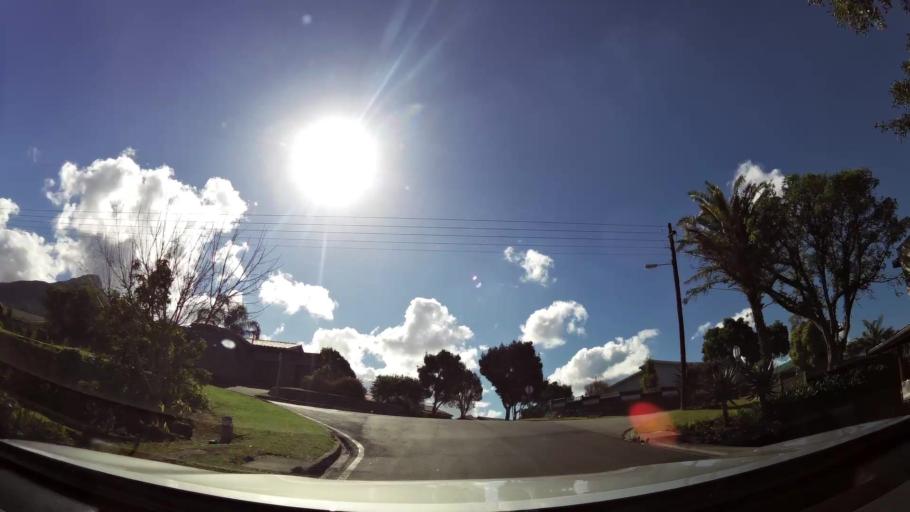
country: ZA
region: Western Cape
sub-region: Eden District Municipality
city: George
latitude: -33.9460
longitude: 22.4771
